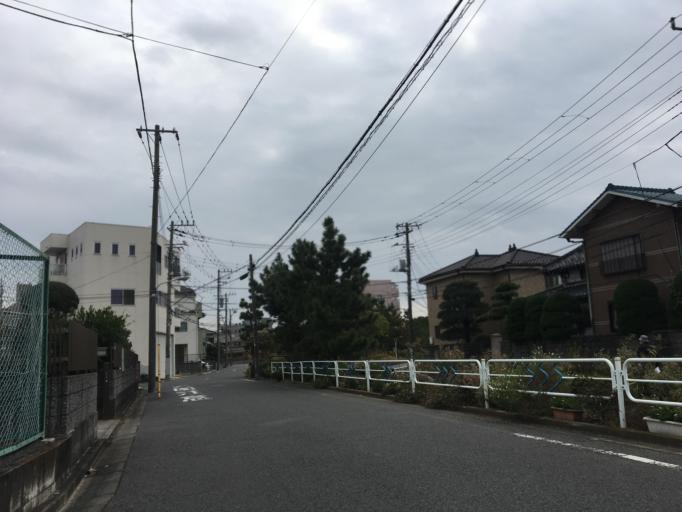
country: JP
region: Tokyo
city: Urayasu
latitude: 35.6532
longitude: 139.8776
